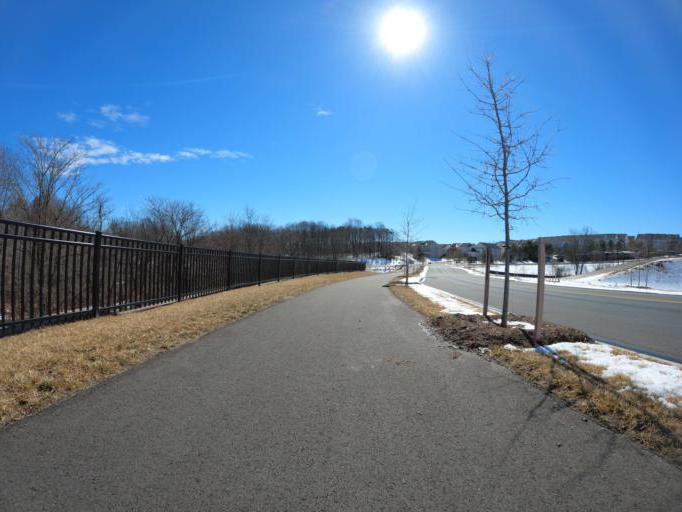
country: US
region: Maryland
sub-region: Montgomery County
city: Clarksburg
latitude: 39.2408
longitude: -77.2732
